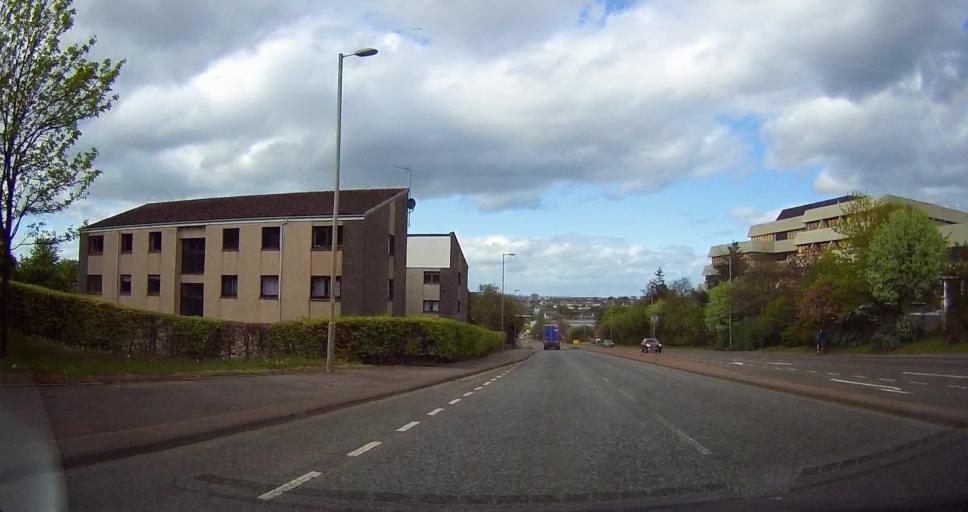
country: GB
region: Scotland
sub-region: Aberdeen City
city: Aberdeen
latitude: 57.1199
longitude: -2.0887
